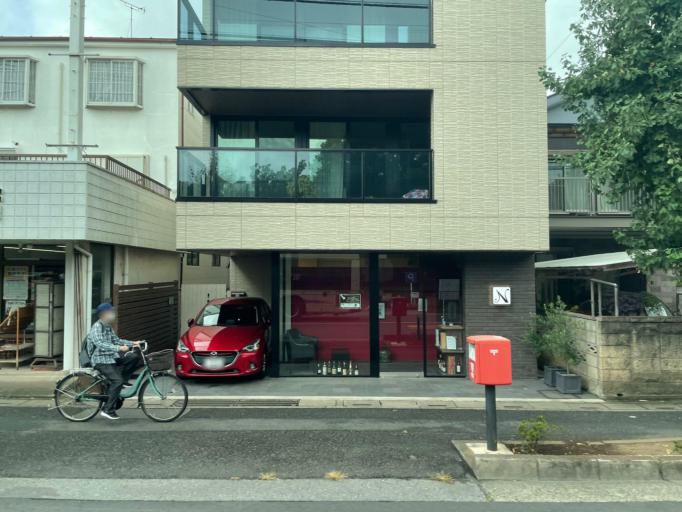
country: JP
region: Saitama
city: Asaka
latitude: 35.7949
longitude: 139.5897
